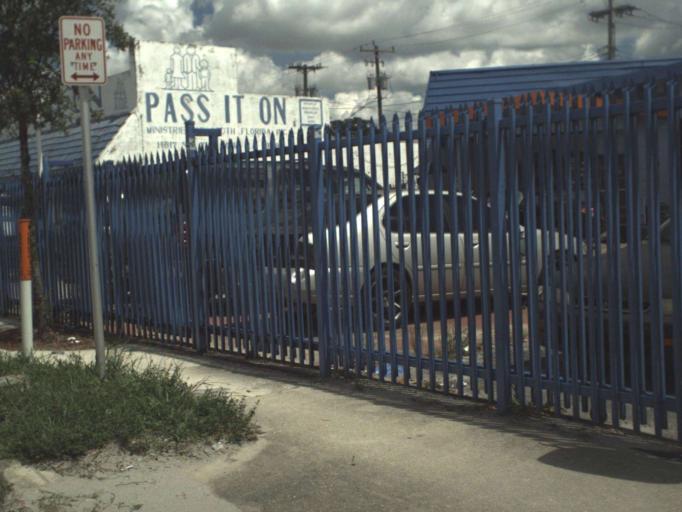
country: US
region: Florida
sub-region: Miami-Dade County
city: Golden Glades
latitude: 25.9086
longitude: -80.2115
